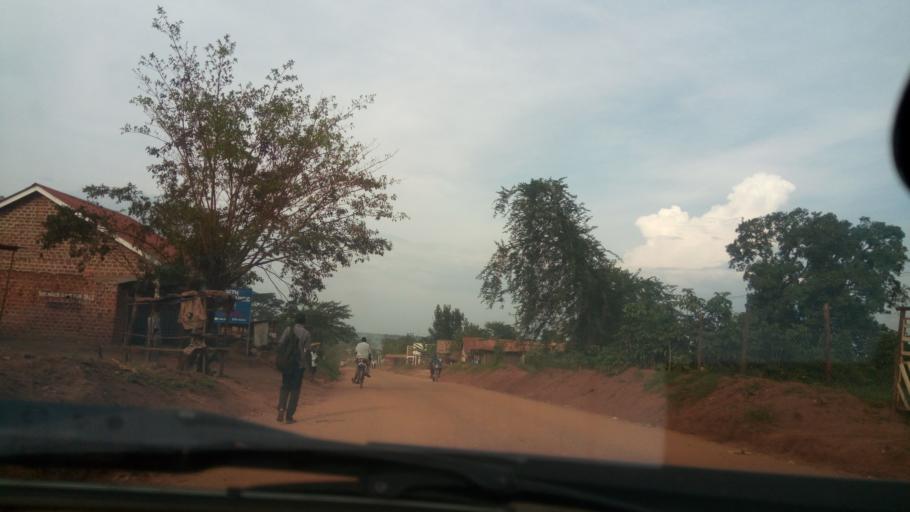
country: UG
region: Central Region
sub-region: Mityana District
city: Mityana
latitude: 0.5594
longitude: 32.1966
